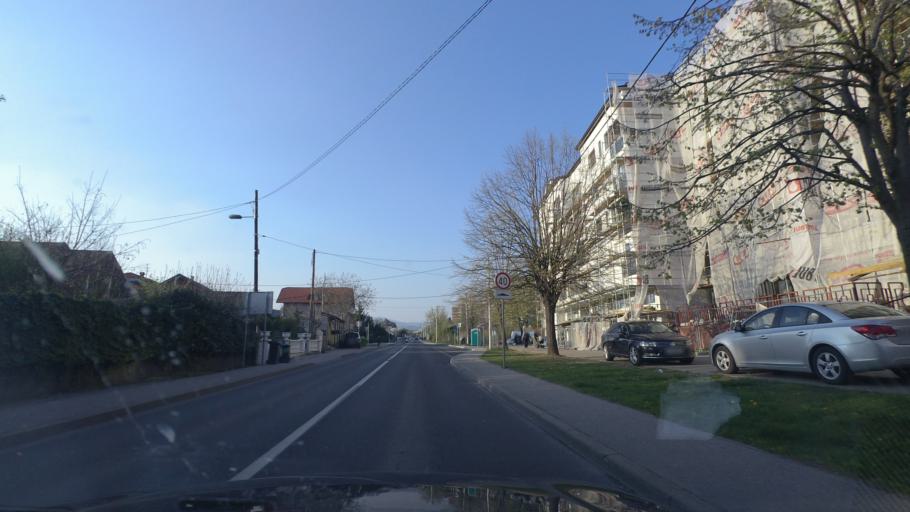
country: HR
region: Grad Zagreb
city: Dubrava
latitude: 45.8247
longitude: 16.0637
